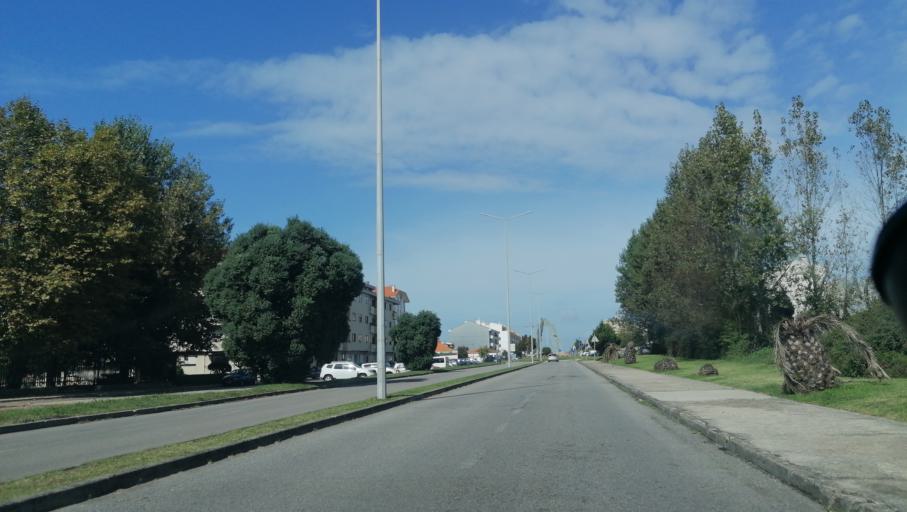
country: PT
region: Aveiro
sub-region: Espinho
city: Espinho
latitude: 41.0026
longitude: -8.6343
